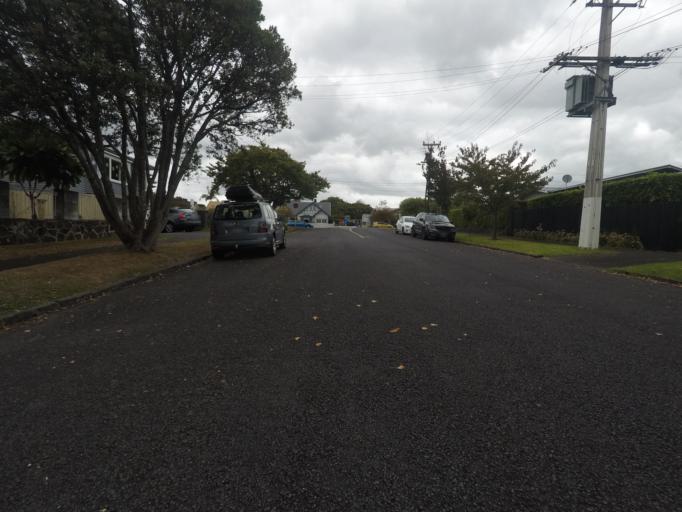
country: NZ
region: Auckland
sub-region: Auckland
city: Auckland
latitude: -36.8751
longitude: 174.7196
